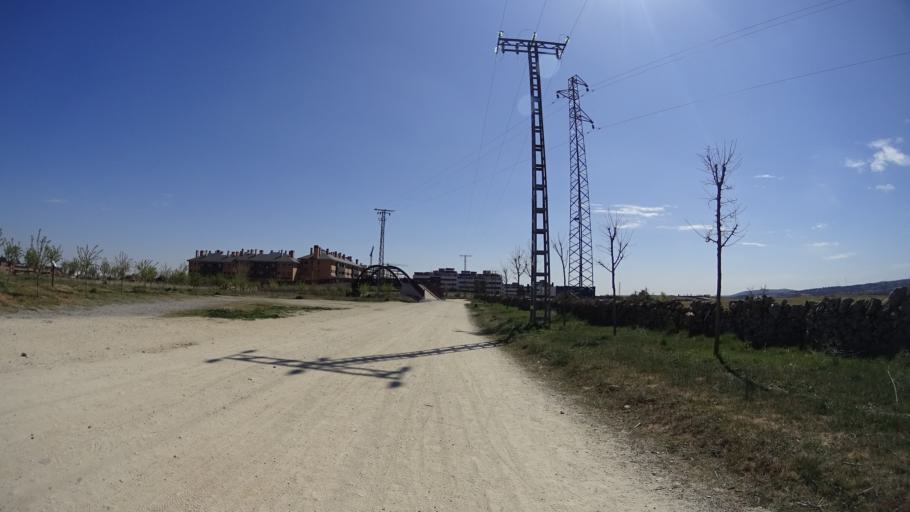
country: ES
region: Madrid
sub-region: Provincia de Madrid
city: Colmenar Viejo
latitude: 40.6536
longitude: -3.7902
